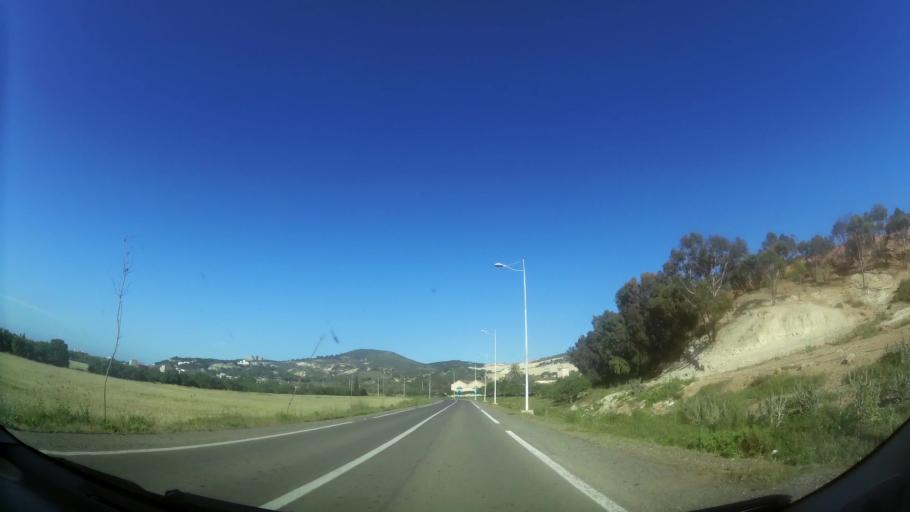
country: MA
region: Oriental
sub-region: Berkane-Taourirt
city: Madagh
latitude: 35.0650
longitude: -2.2208
